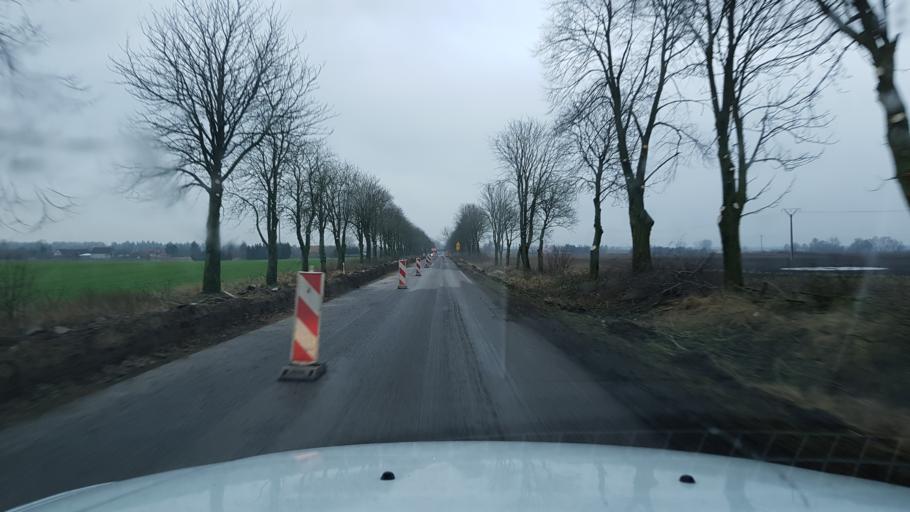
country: PL
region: West Pomeranian Voivodeship
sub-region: Powiat gryficki
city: Ploty
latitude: 53.8261
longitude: 15.2482
